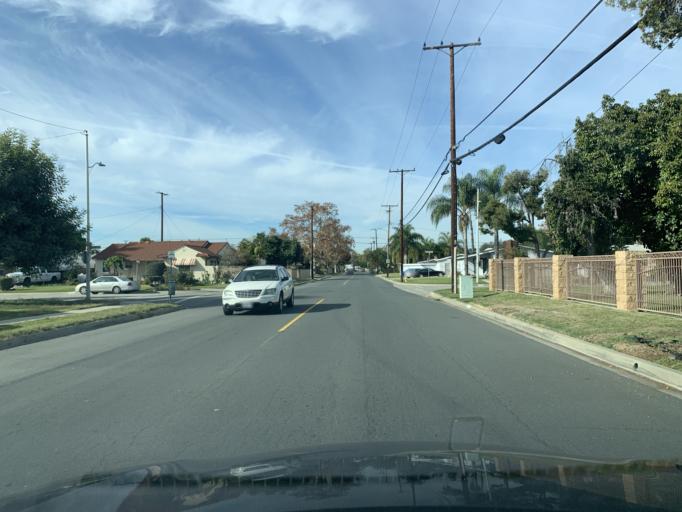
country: US
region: California
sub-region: Los Angeles County
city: West Covina
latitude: 34.0755
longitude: -117.9306
